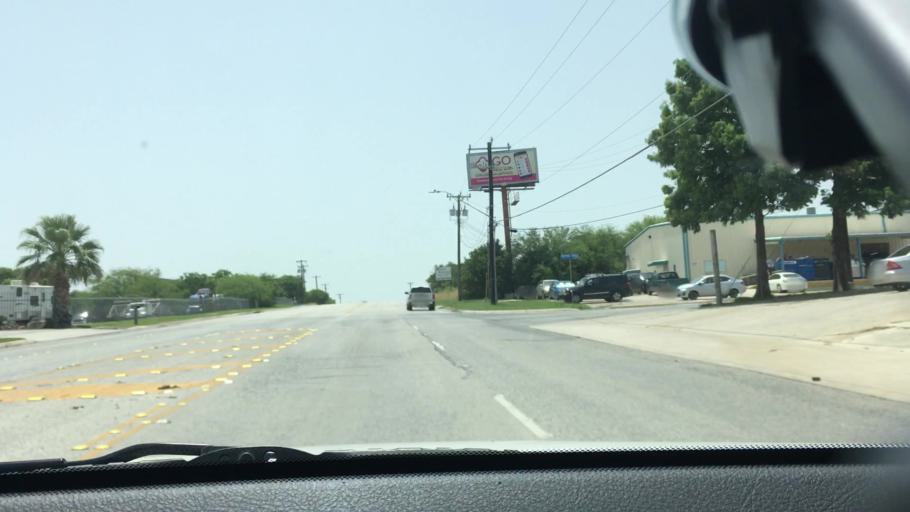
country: US
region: Texas
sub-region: Bexar County
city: Live Oak
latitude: 29.5671
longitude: -98.3546
